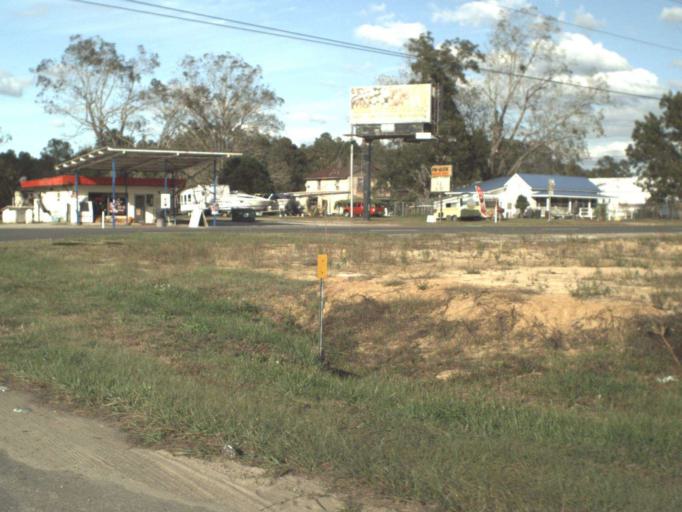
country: US
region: Florida
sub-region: Washington County
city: Chipley
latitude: 30.7755
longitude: -85.5669
